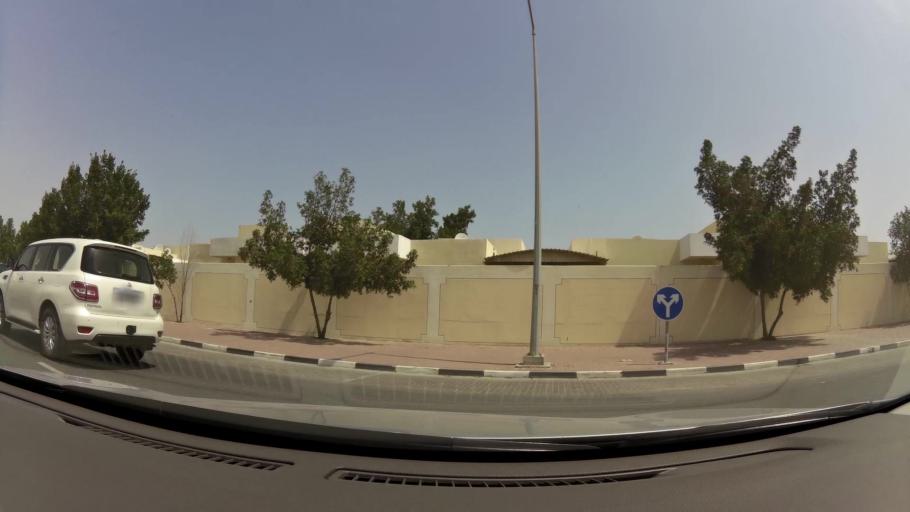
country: QA
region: Baladiyat ad Dawhah
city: Doha
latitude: 25.3244
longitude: 51.4891
